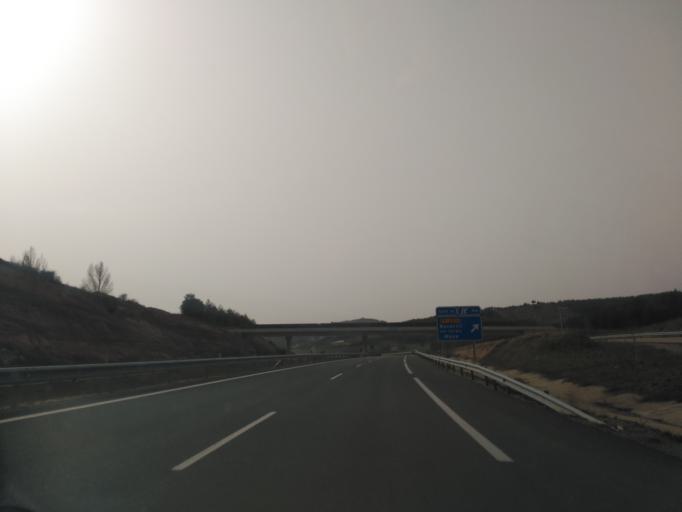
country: ES
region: Castille and Leon
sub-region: Provincia de Palencia
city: Alar del Rey
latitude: 42.7266
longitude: -4.2889
